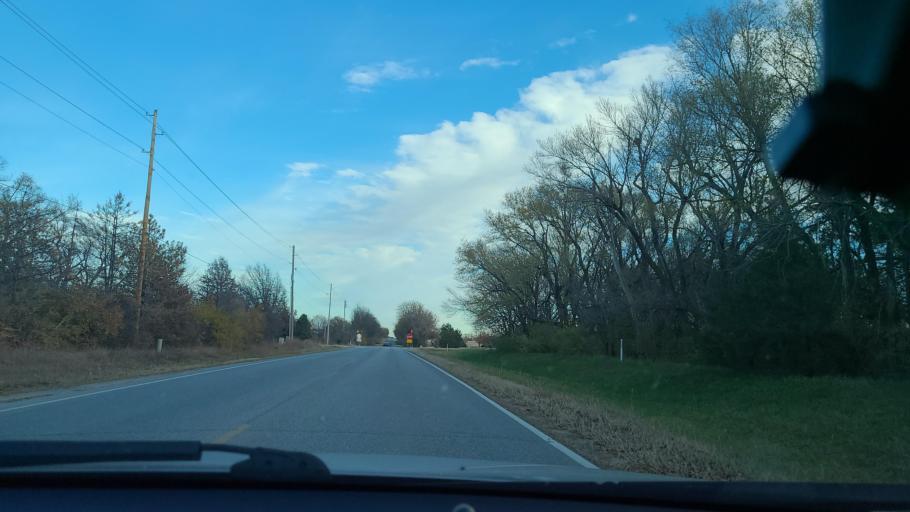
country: US
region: Kansas
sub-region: Sedgwick County
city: Goddard
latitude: 37.6497
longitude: -97.5549
